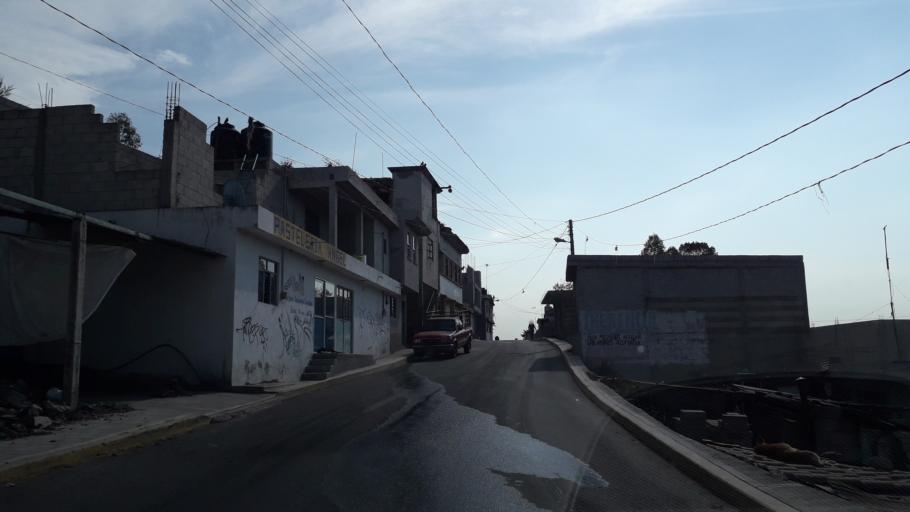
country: MX
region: Puebla
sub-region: Puebla
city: San Andres Azumiatla
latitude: 18.9046
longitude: -98.2528
